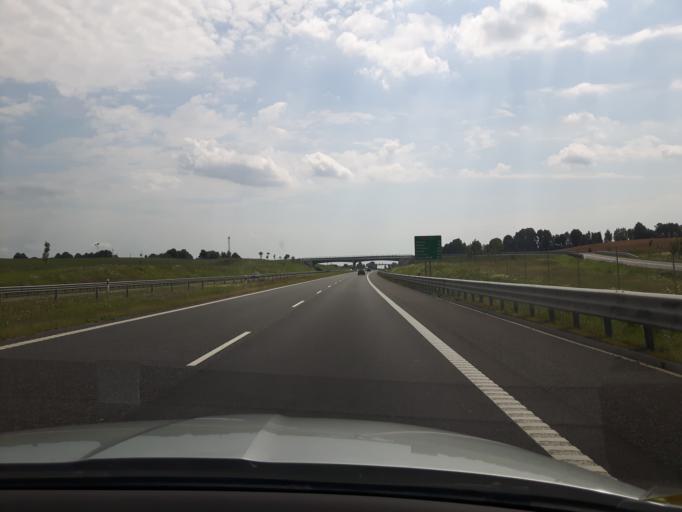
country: PL
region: Warmian-Masurian Voivodeship
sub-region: Powiat olsztynski
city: Olsztynek
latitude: 53.4927
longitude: 20.3172
